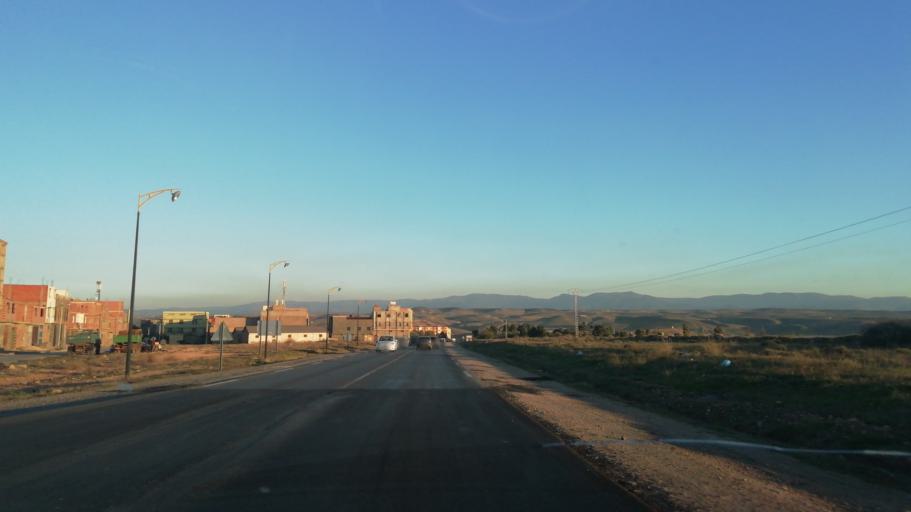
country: DZ
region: Tlemcen
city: Nedroma
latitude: 34.8922
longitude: -1.6592
